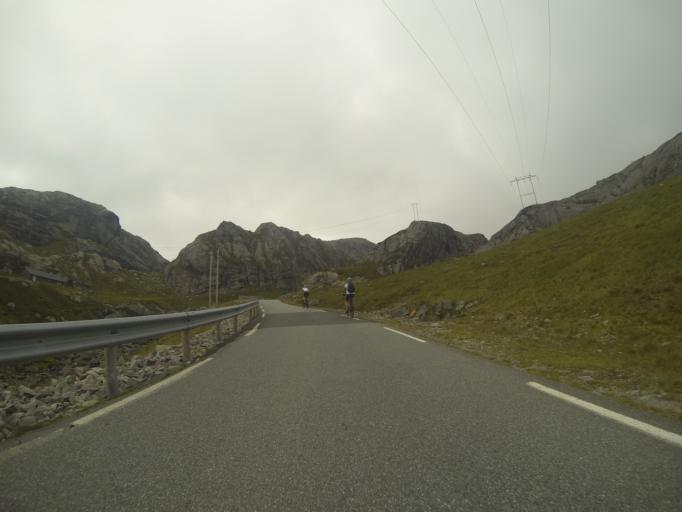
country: NO
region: Vest-Agder
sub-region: Sirdal
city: Tonstad
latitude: 59.0326
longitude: 6.6539
